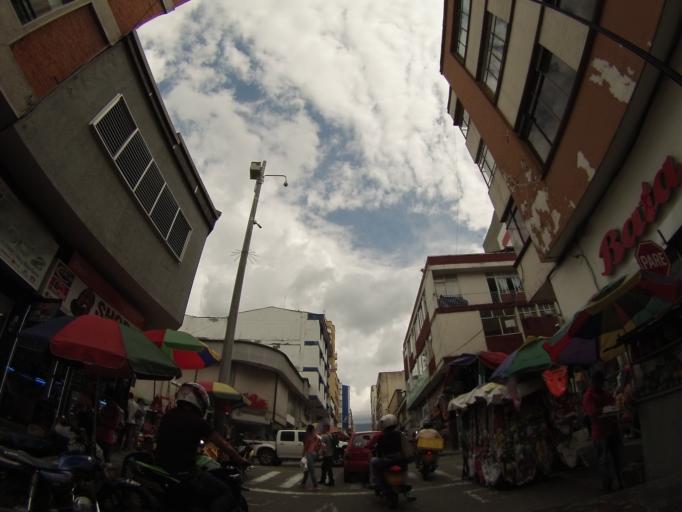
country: CO
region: Quindio
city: Armenia
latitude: 4.5345
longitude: -75.6734
